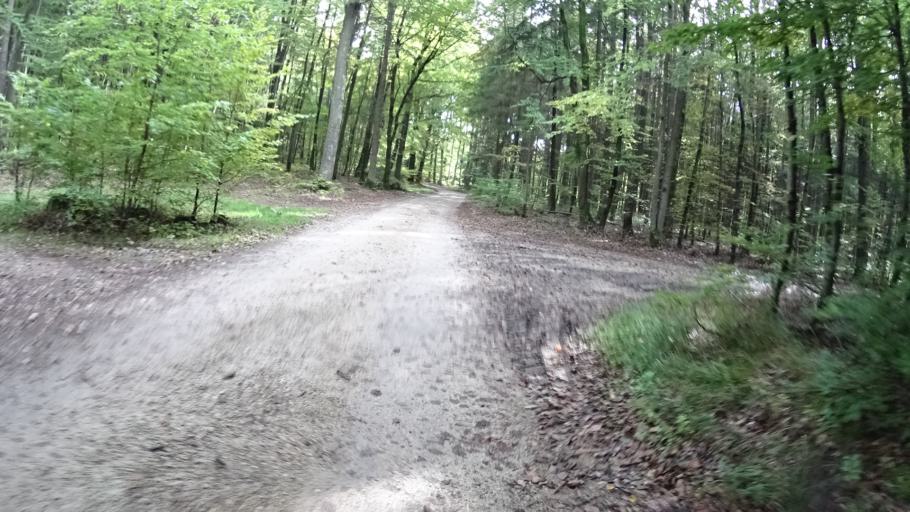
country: DE
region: Bavaria
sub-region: Upper Bavaria
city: Walting
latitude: 48.9177
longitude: 11.3251
